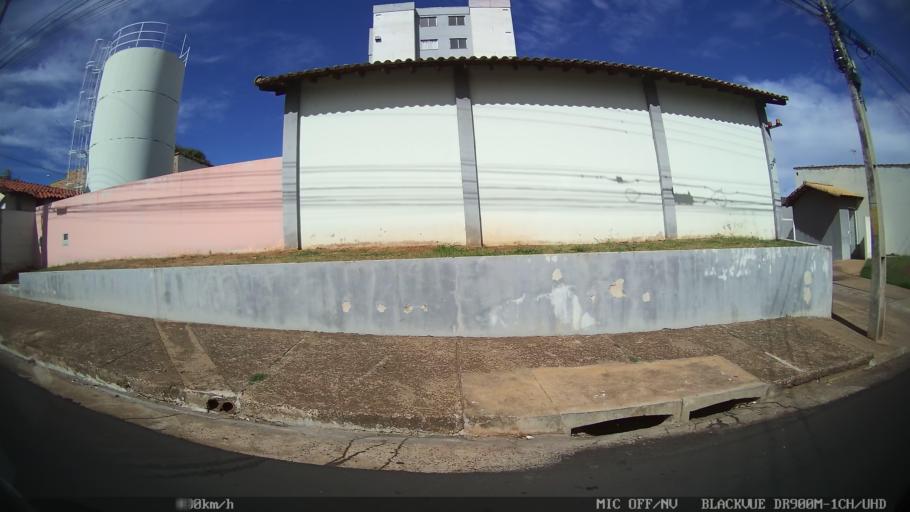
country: BR
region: Sao Paulo
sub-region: Catanduva
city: Catanduva
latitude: -21.1263
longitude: -48.9575
